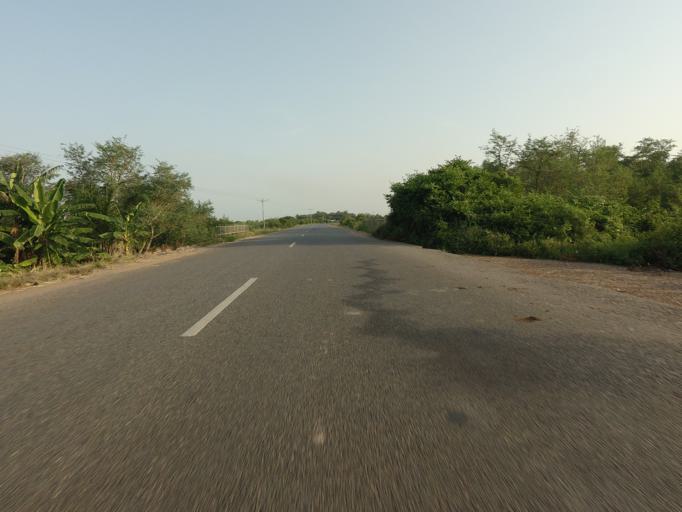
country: GH
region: Volta
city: Anloga
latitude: 5.9747
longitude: 0.6662
